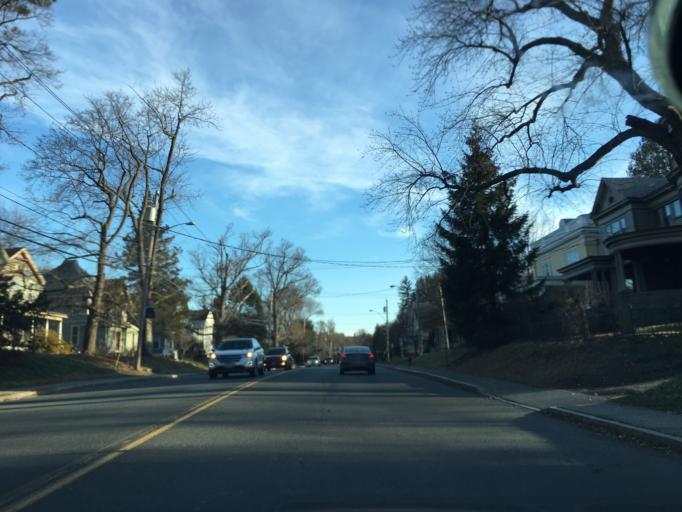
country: US
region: New York
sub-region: Rensselaer County
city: Troy
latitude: 42.7177
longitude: -73.6711
